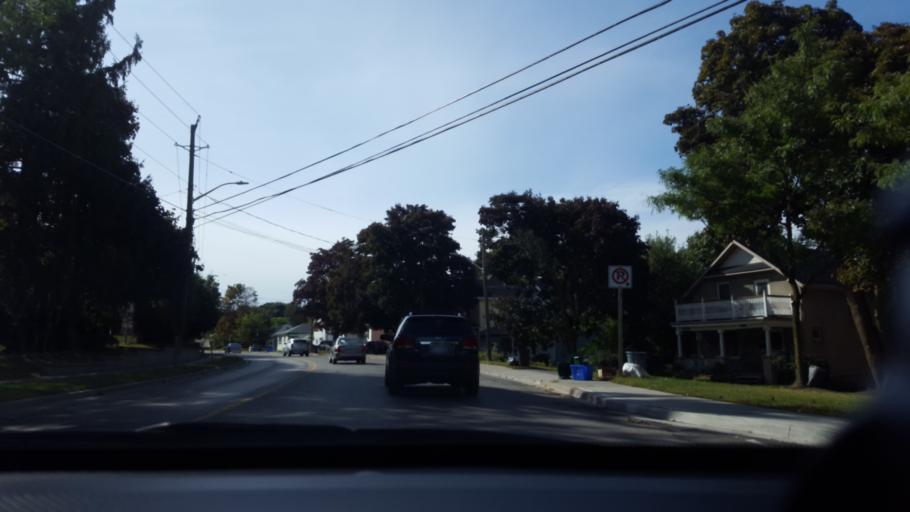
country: CA
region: Ontario
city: Newmarket
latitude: 44.0481
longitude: -79.4533
